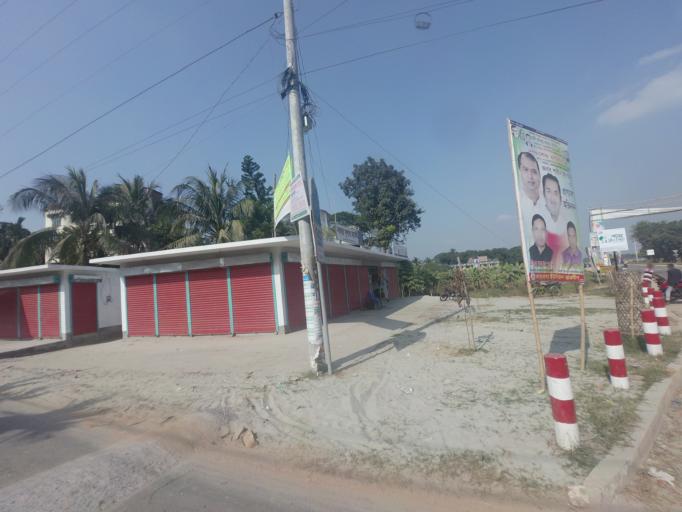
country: BD
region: Dhaka
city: Azimpur
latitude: 23.7319
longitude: 90.3225
